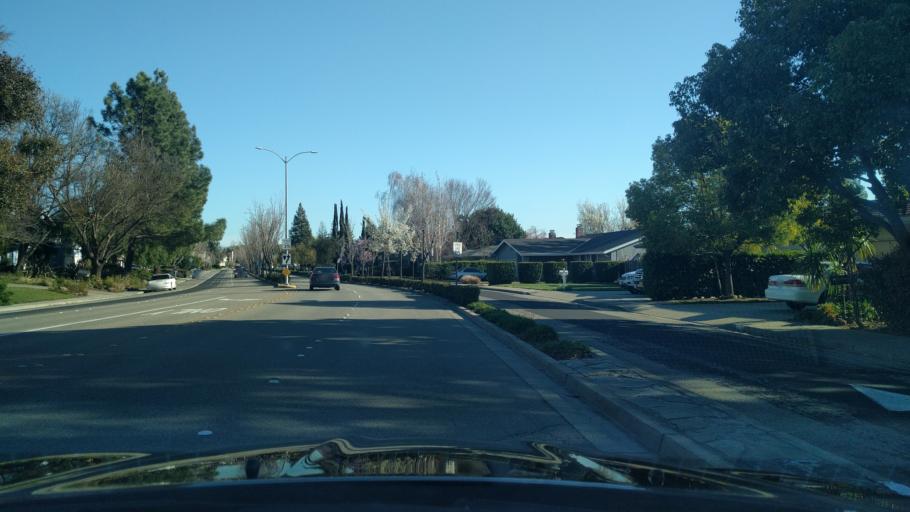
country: US
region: California
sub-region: Alameda County
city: Dublin
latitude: 37.7441
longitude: -121.9307
